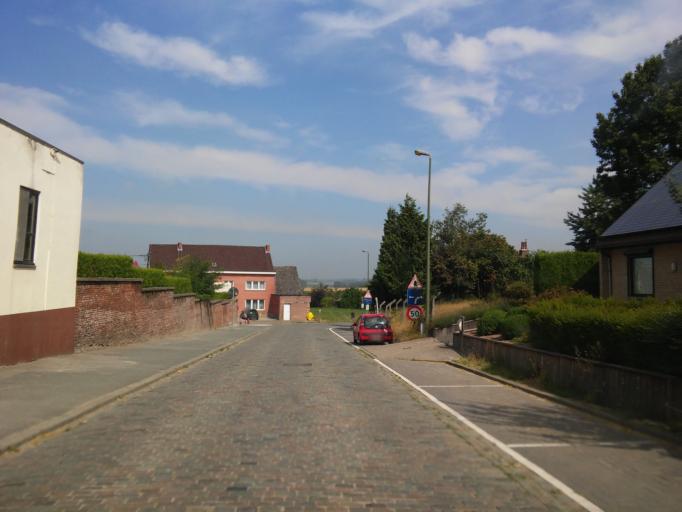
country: BE
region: Flanders
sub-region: Provincie Vlaams-Brabant
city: Pepingen
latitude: 50.7357
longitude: 4.1118
